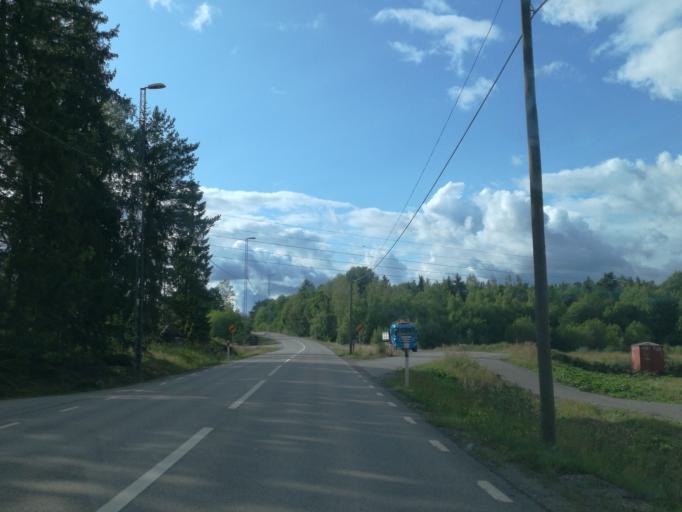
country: SE
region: Stockholm
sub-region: Upplands Vasby Kommun
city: Upplands Vaesby
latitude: 59.5307
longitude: 17.9824
